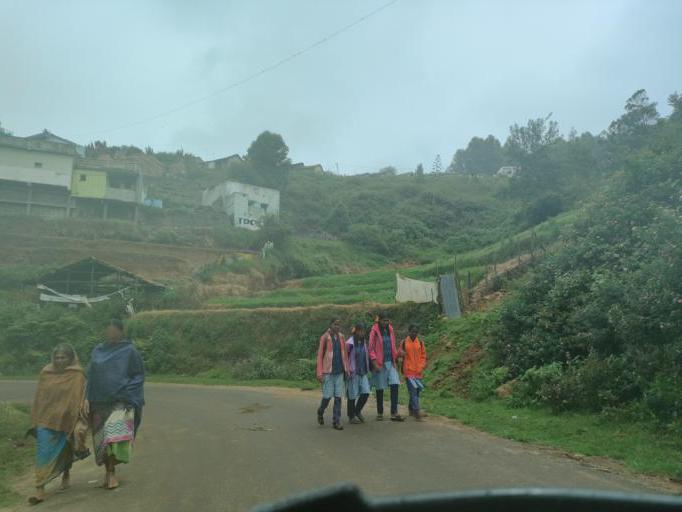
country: IN
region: Tamil Nadu
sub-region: Dindigul
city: Kodaikanal
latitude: 10.2232
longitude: 77.3465
